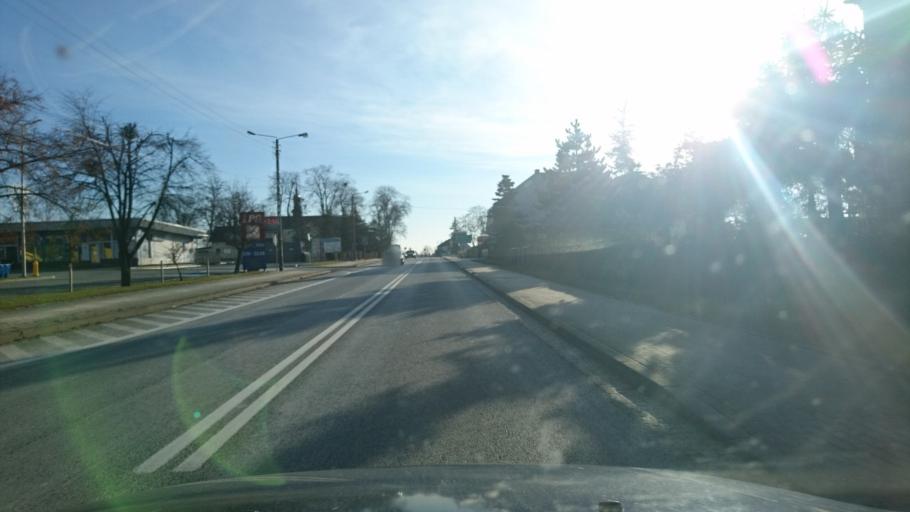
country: PL
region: Opole Voivodeship
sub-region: Powiat oleski
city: Dalachow
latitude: 51.0407
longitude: 18.5975
